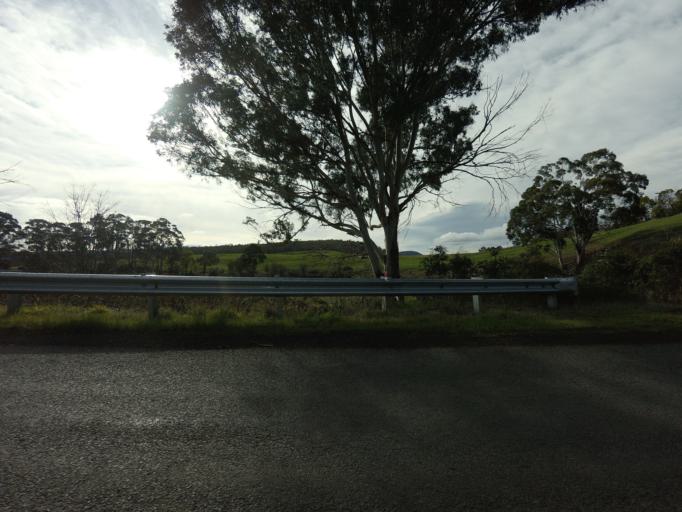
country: AU
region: Tasmania
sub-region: Derwent Valley
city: New Norfolk
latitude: -42.7828
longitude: 146.9942
